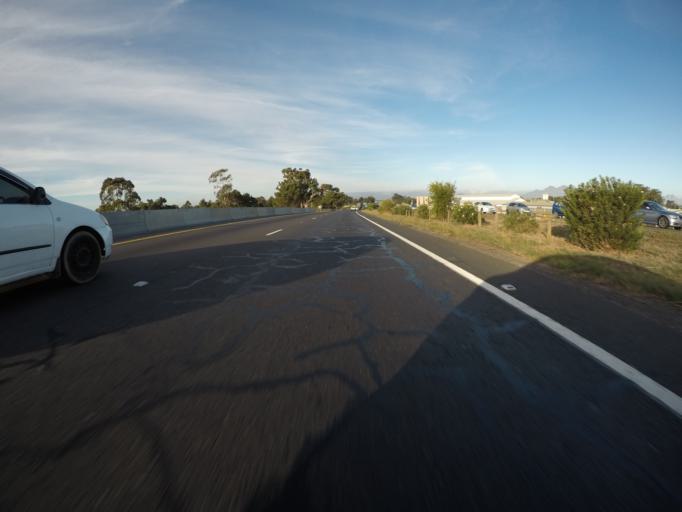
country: ZA
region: Western Cape
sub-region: City of Cape Town
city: Kraaifontein
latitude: -33.8381
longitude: 18.7265
